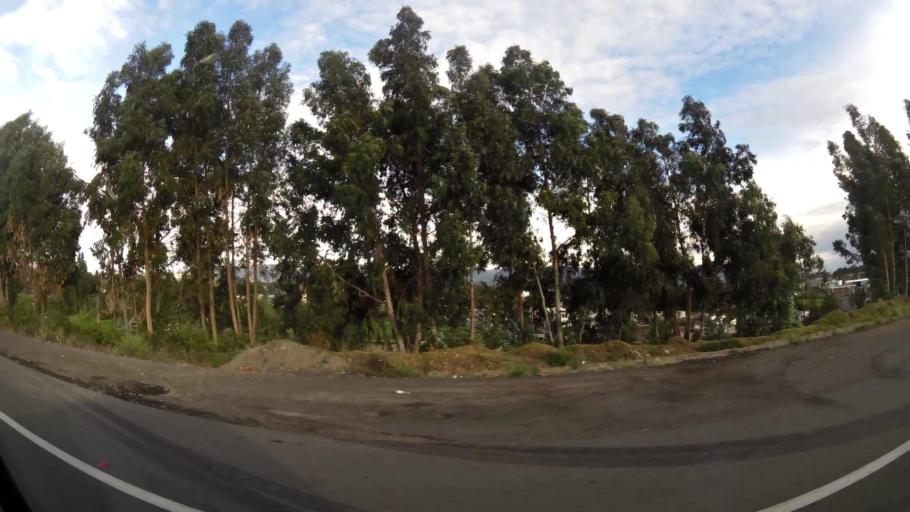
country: EC
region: Cotopaxi
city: Saquisili
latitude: -0.8625
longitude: -78.6244
